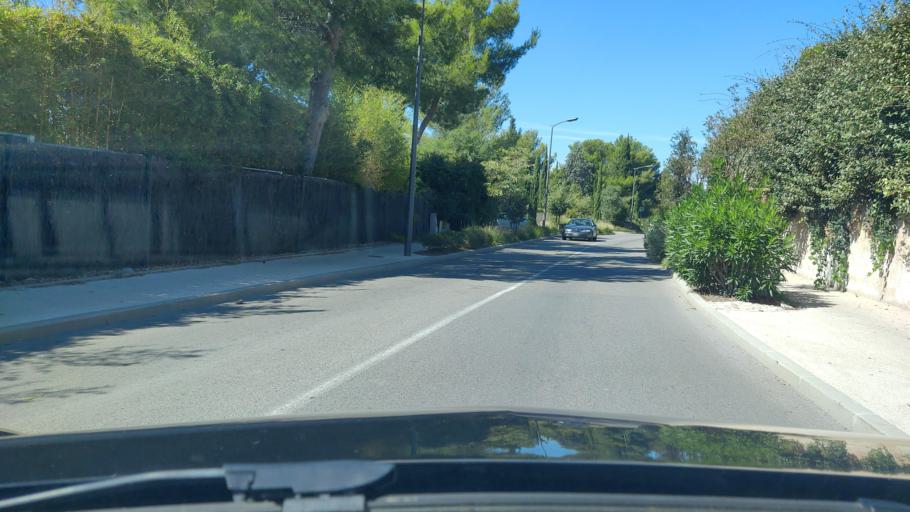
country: FR
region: Provence-Alpes-Cote d'Azur
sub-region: Departement du Var
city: Sanary-sur-Mer
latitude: 43.1356
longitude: 5.7878
